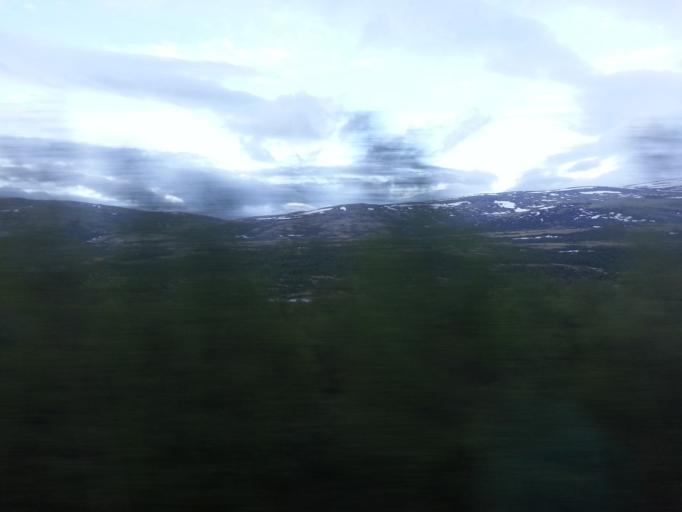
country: NO
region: Oppland
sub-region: Dovre
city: Dovre
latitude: 62.1988
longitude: 9.5143
